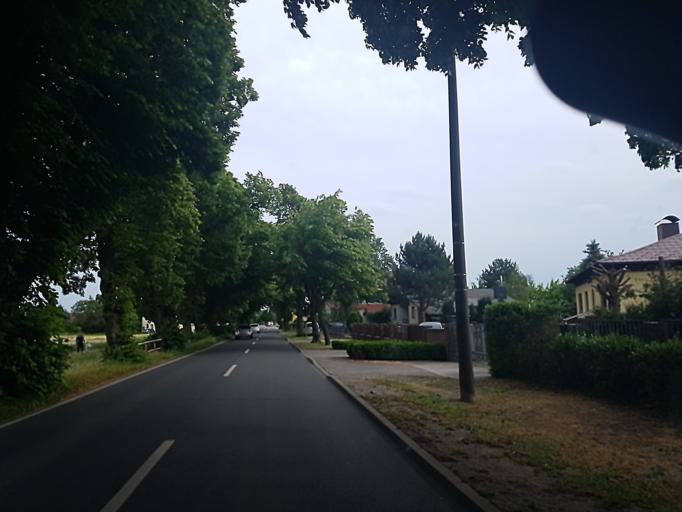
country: DE
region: Saxony-Anhalt
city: Wittenburg
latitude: 51.8807
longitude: 12.6303
